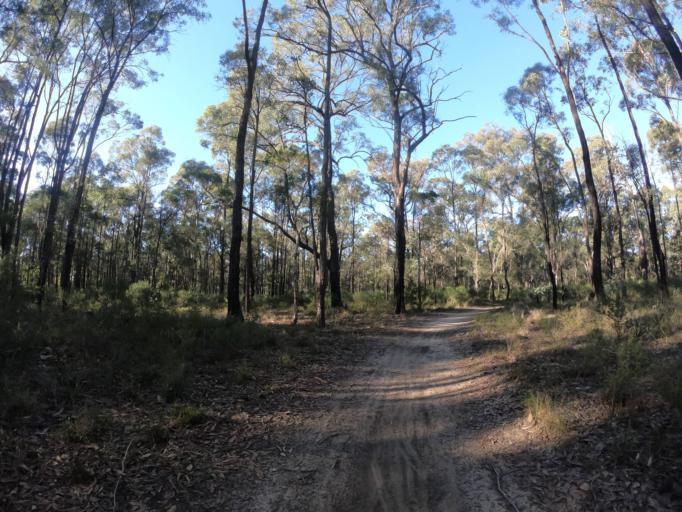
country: AU
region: New South Wales
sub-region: Hawkesbury
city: South Windsor
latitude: -33.6425
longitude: 150.7962
